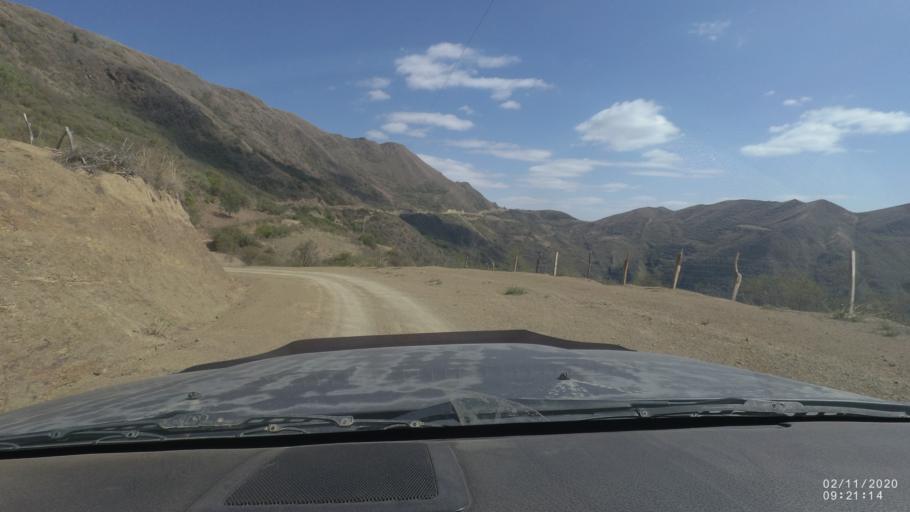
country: BO
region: Chuquisaca
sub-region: Provincia Zudanez
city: Mojocoya
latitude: -18.4769
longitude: -64.5796
